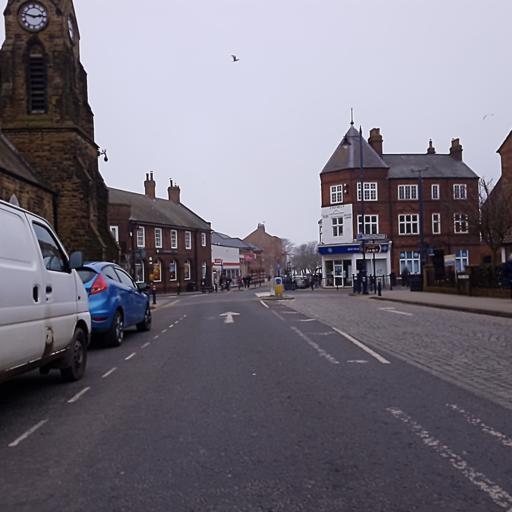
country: GB
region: England
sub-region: North Yorkshire
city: Filey
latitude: 54.2098
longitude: -0.2894
